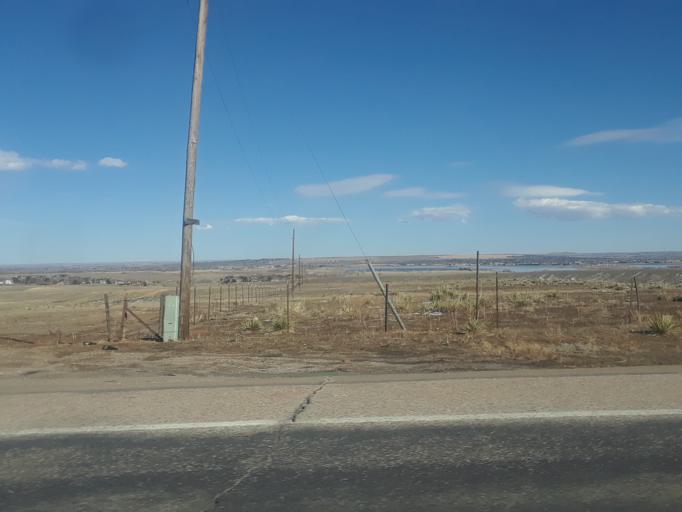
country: US
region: Colorado
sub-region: Boulder County
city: Boulder
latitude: 40.0874
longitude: -105.2822
